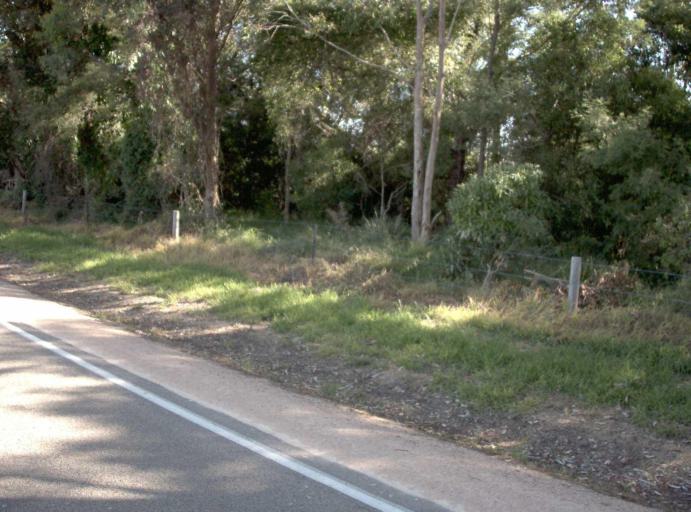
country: AU
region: Victoria
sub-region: East Gippsland
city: Lakes Entrance
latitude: -37.7384
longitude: 148.5052
